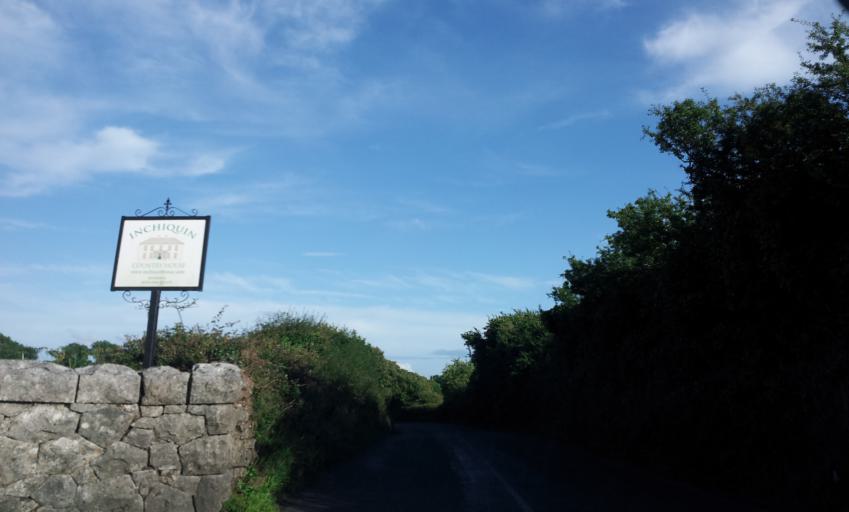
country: IE
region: Munster
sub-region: An Clar
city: Ennis
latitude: 52.9562
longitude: -9.0747
